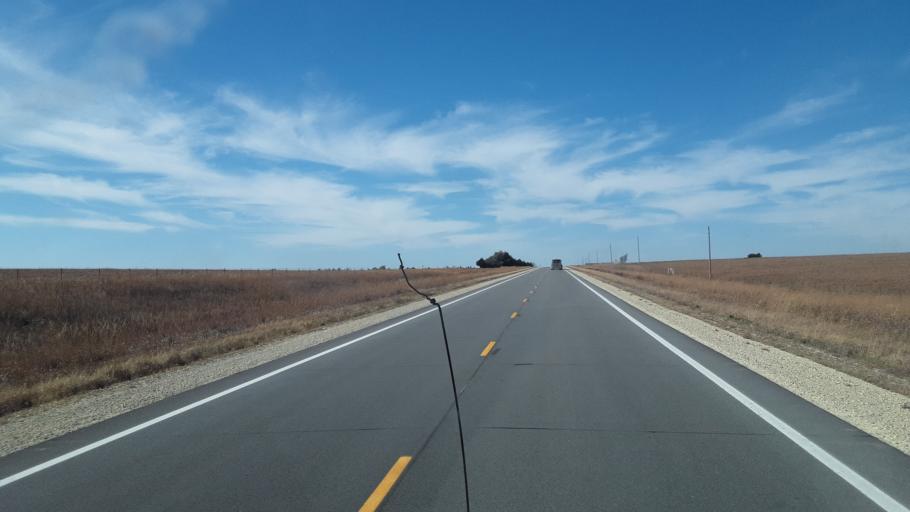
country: US
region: Kansas
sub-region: Marion County
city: Marion
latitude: 38.3628
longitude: -96.7915
